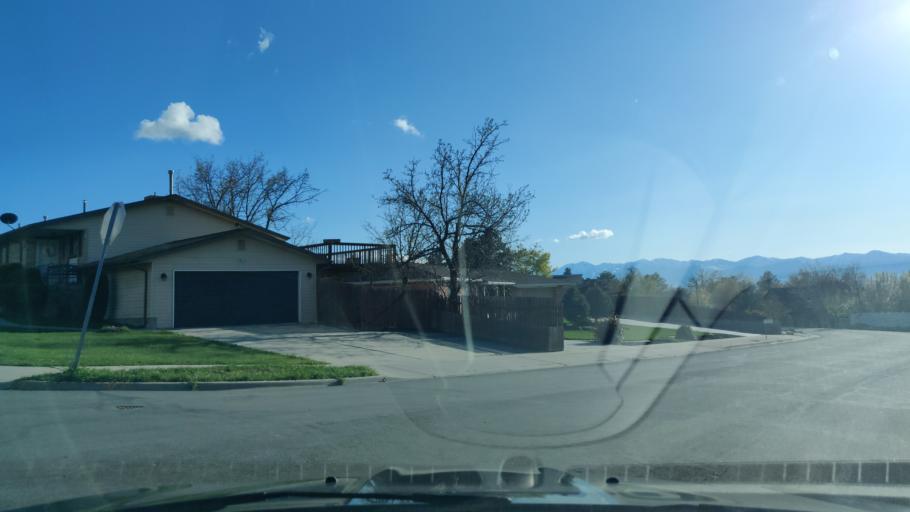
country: US
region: Utah
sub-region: Salt Lake County
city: Little Cottonwood Creek Valley
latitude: 40.6167
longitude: -111.8249
